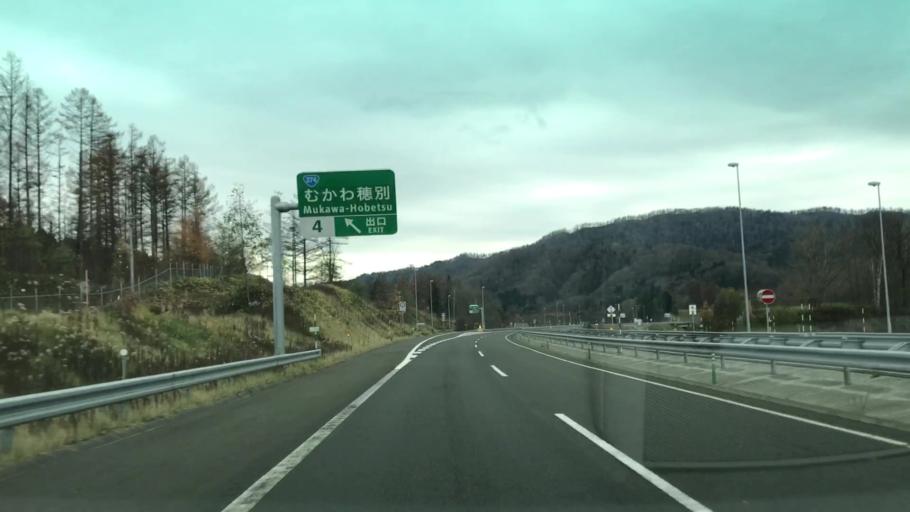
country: JP
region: Hokkaido
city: Shimo-furano
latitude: 42.9209
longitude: 142.1995
